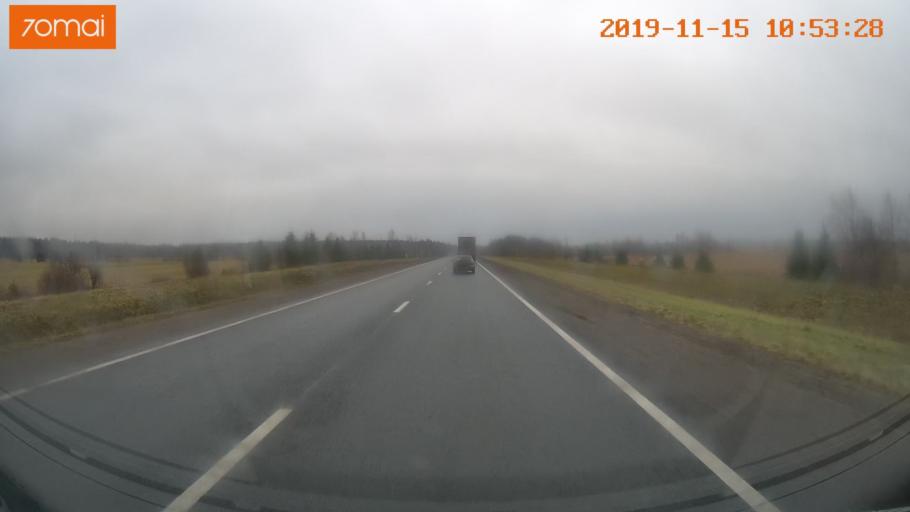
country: RU
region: Vologda
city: Chebsara
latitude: 59.1691
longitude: 38.7550
